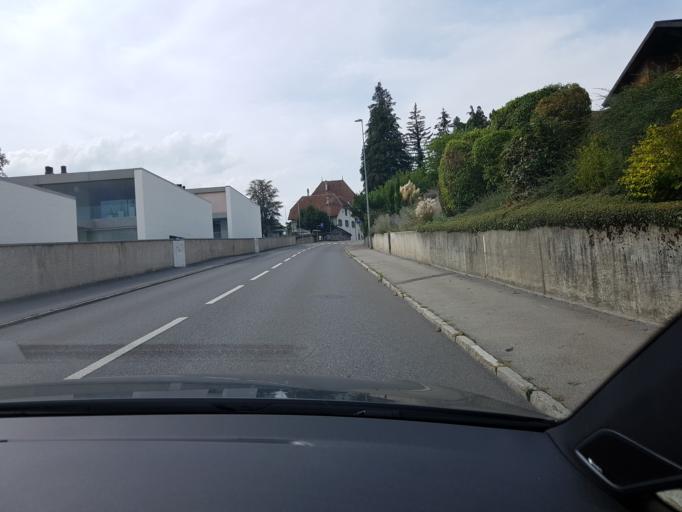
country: CH
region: Bern
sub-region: Thun District
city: Hilterfingen
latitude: 46.7282
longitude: 7.6740
